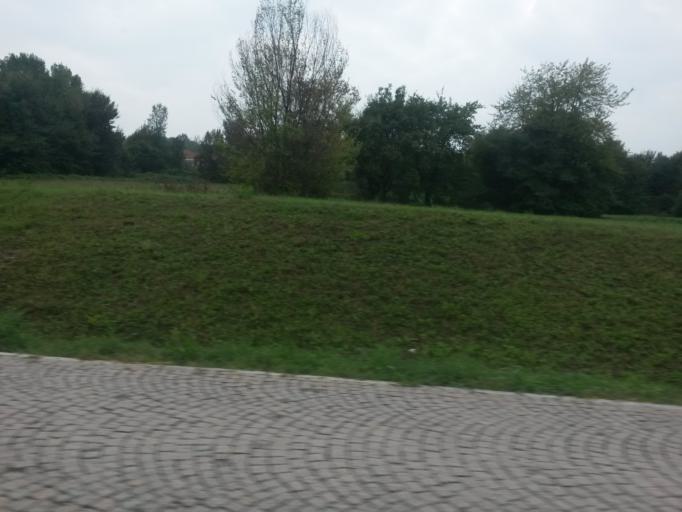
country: IT
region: Piedmont
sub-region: Provincia di Torino
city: Buttigliera Alta
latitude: 45.0665
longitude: 7.4427
